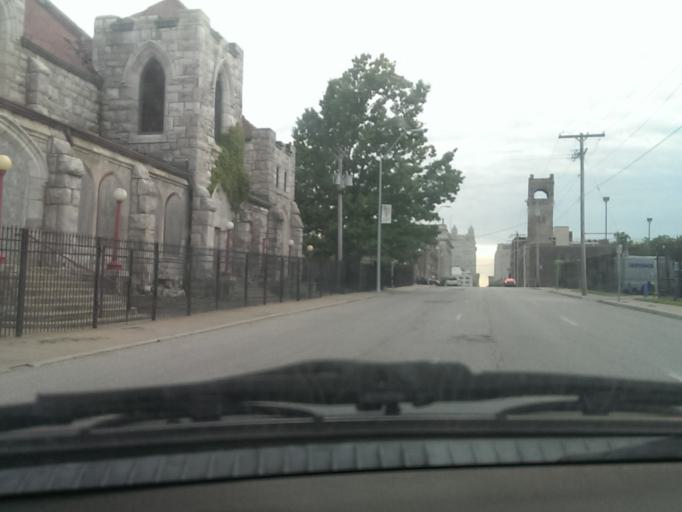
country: US
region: Missouri
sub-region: Jackson County
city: Kansas City
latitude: 39.1031
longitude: -94.5686
